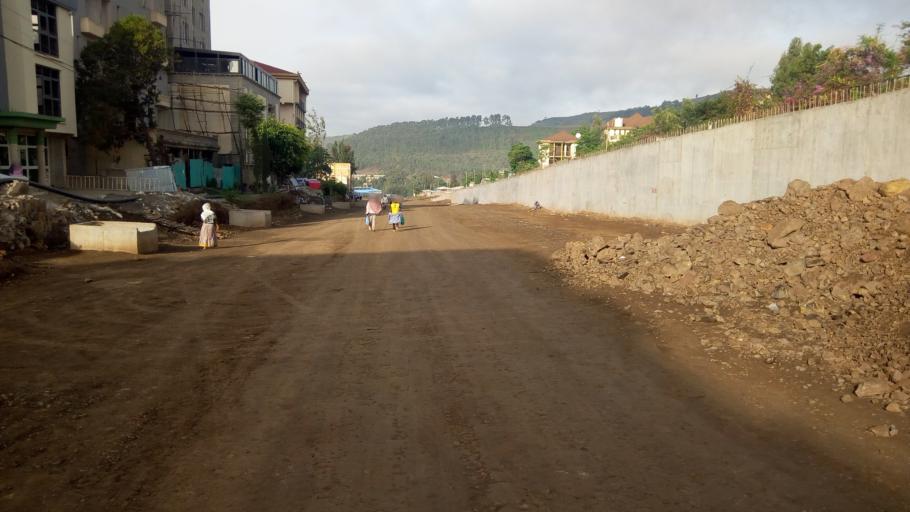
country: ET
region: Amhara
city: Gondar
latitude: 12.5889
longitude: 37.4393
